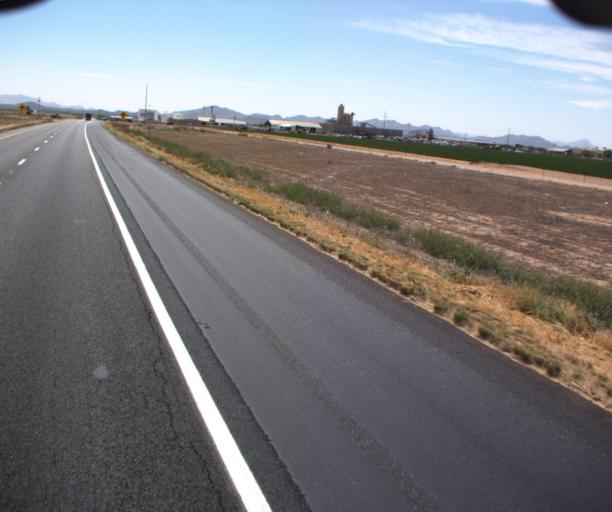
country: US
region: Arizona
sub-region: Maricopa County
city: Buckeye
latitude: 33.3809
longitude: -112.6265
